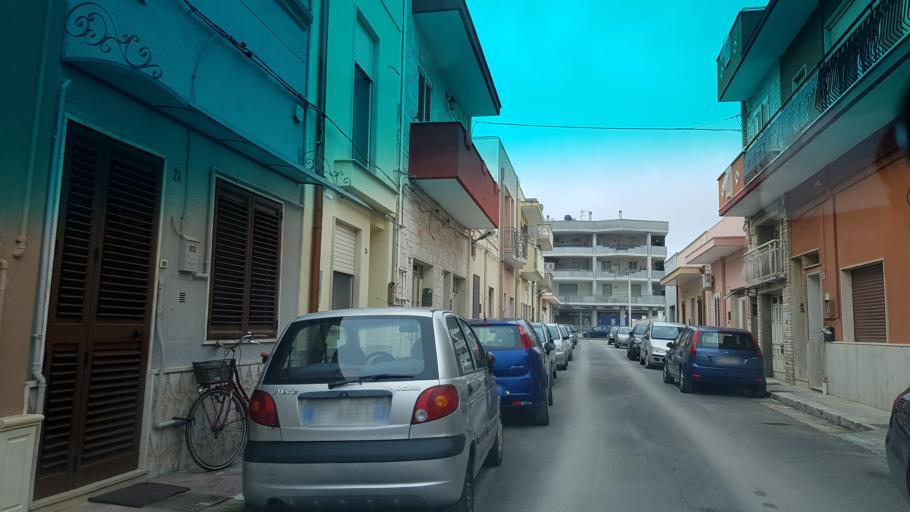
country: IT
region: Apulia
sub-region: Provincia di Brindisi
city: Mesagne
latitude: 40.5603
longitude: 17.7960
